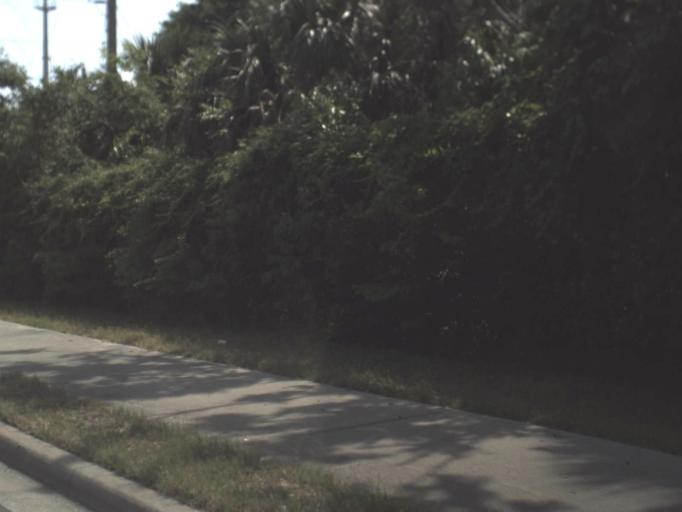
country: US
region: Florida
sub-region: Duval County
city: Atlantic Beach
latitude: 30.3723
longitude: -81.4104
